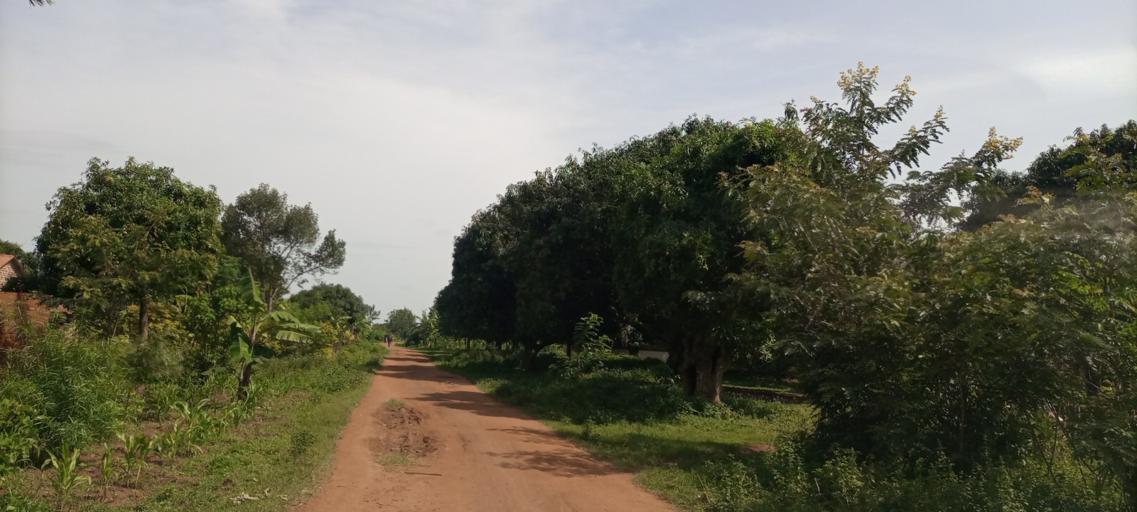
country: UG
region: Eastern Region
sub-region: Mbale District
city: Mbale
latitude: 1.1308
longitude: 34.0231
